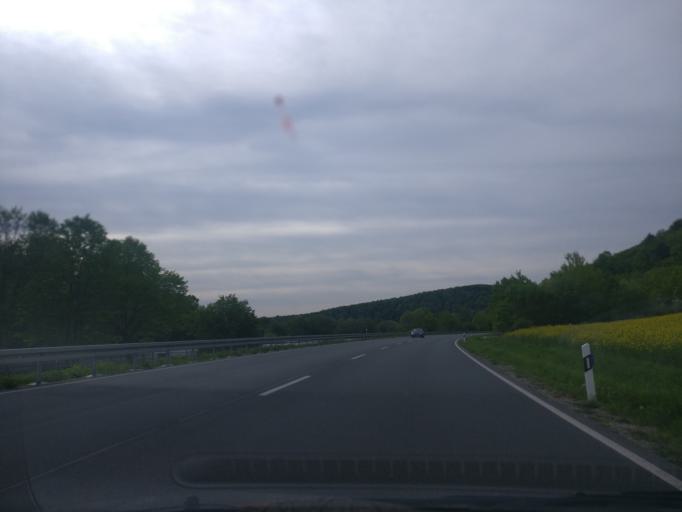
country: DE
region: Hesse
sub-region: Regierungsbezirk Kassel
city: Fuldatal
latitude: 51.3640
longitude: 9.5468
